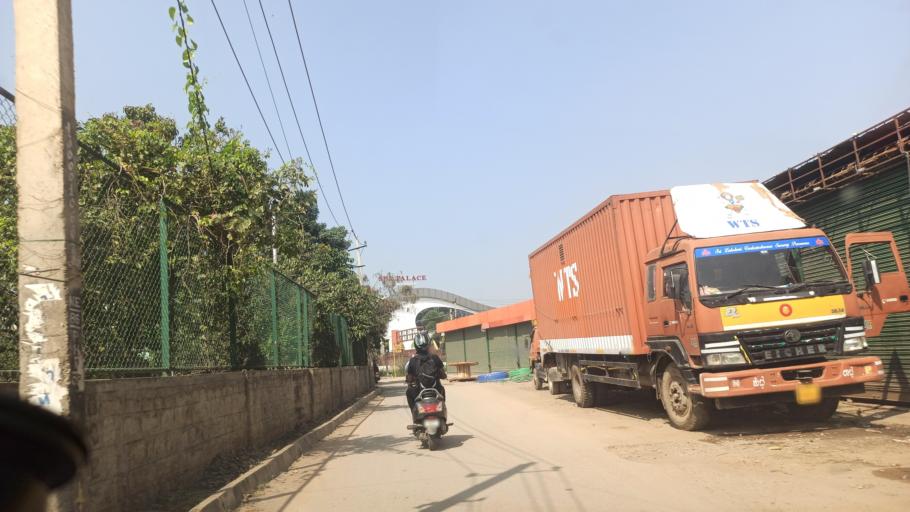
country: IN
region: Karnataka
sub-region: Bangalore Urban
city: Bangalore
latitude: 12.9484
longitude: 77.6979
